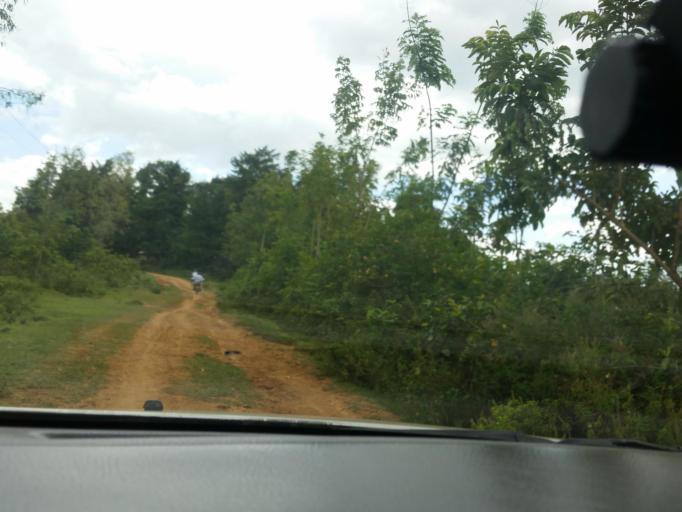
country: KE
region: Kakamega
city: Butere
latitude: 0.1104
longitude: 34.4096
